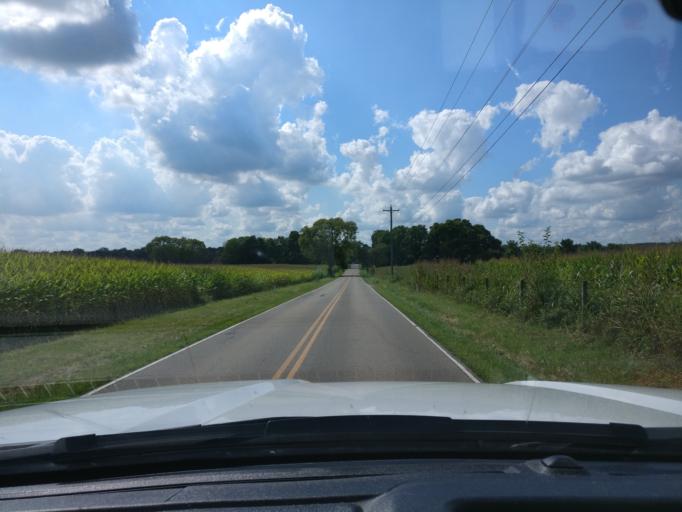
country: US
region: Ohio
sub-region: Warren County
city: Springboro
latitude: 39.5050
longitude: -84.2191
